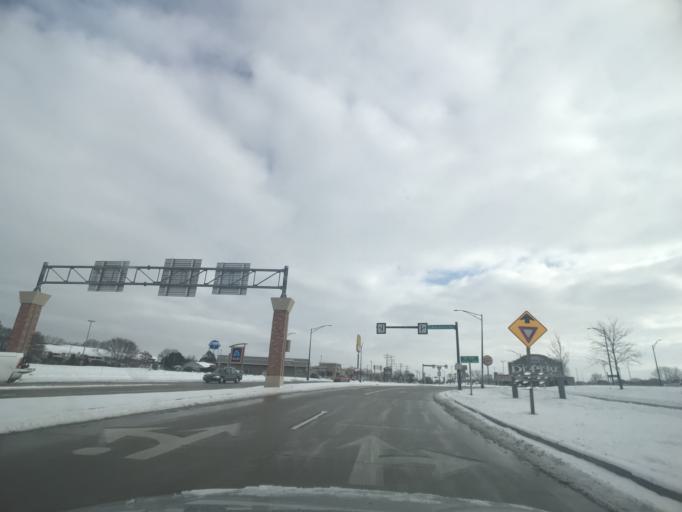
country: US
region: Wisconsin
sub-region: Brown County
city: De Pere
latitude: 44.4521
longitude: -88.0885
